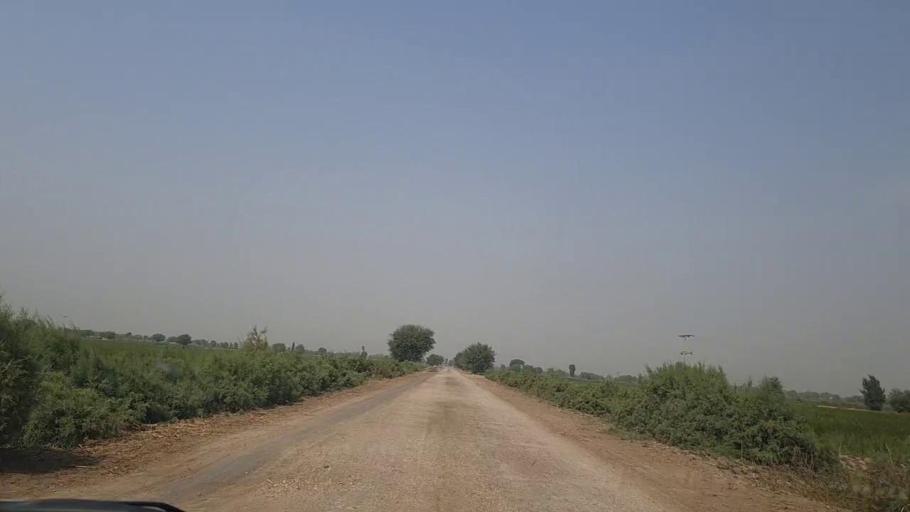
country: PK
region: Sindh
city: Mirpur Khas
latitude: 25.6141
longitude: 69.2009
